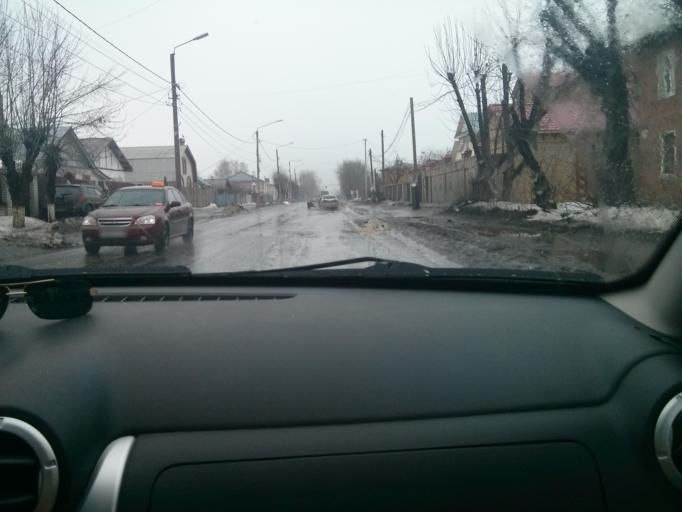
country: RU
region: Vladimir
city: Murom
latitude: 55.5847
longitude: 42.0365
